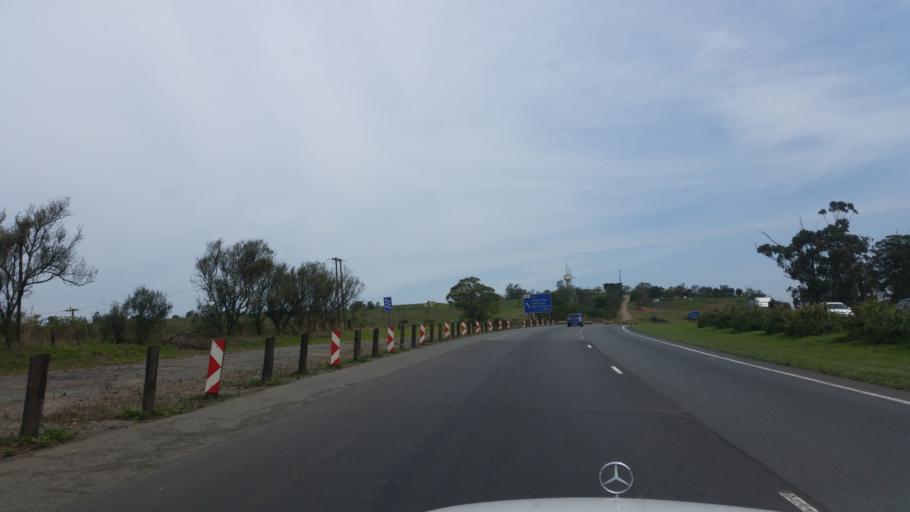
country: ZA
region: KwaZulu-Natal
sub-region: uMgungundlovu District Municipality
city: Camperdown
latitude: -29.7076
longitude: 30.4961
